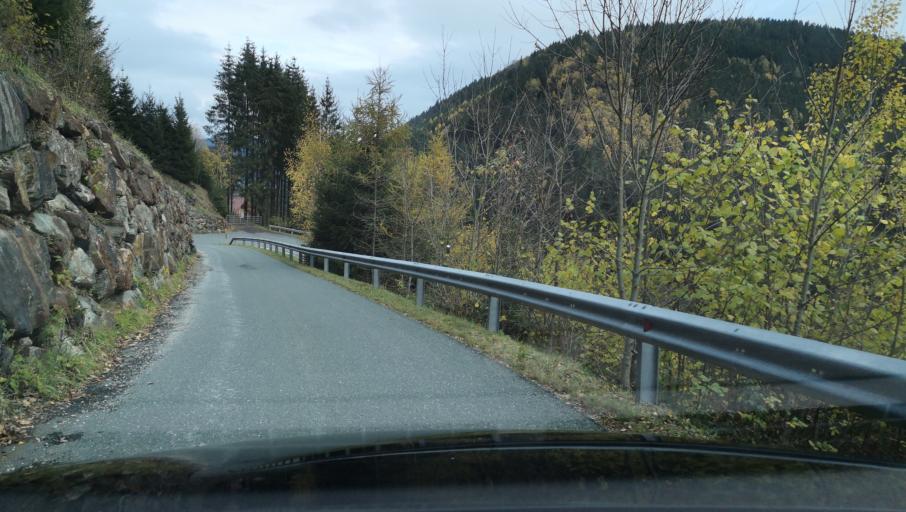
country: AT
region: Styria
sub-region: Politischer Bezirk Weiz
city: Birkfeld
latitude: 47.3657
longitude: 15.6333
